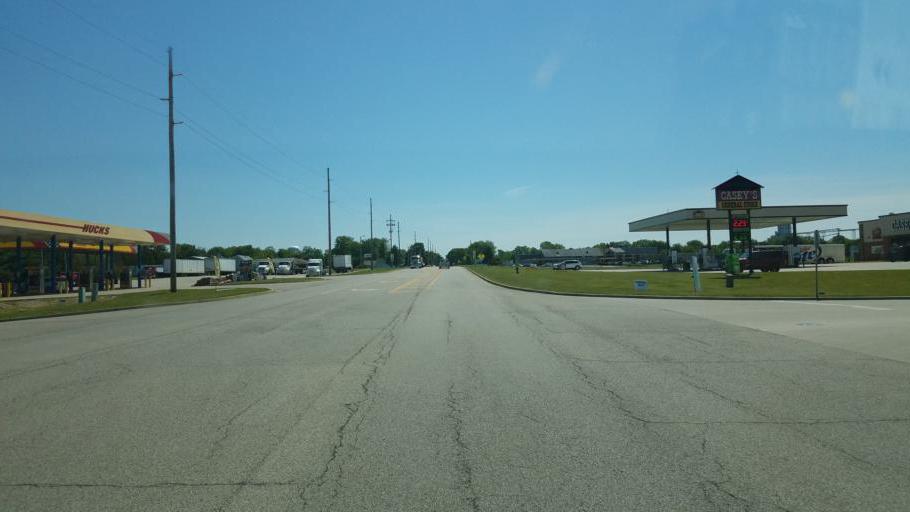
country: US
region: Illinois
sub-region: McLean County
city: Heyworth
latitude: 40.3120
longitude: -88.9864
